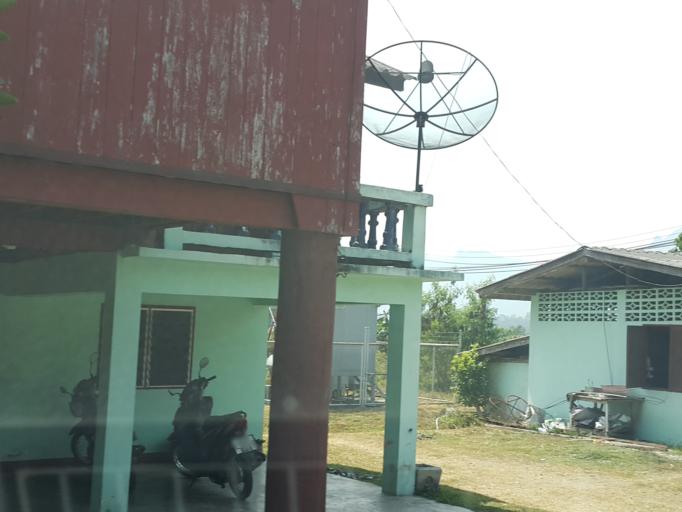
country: TH
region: Lampang
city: Chae Hom
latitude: 18.7570
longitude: 99.5684
